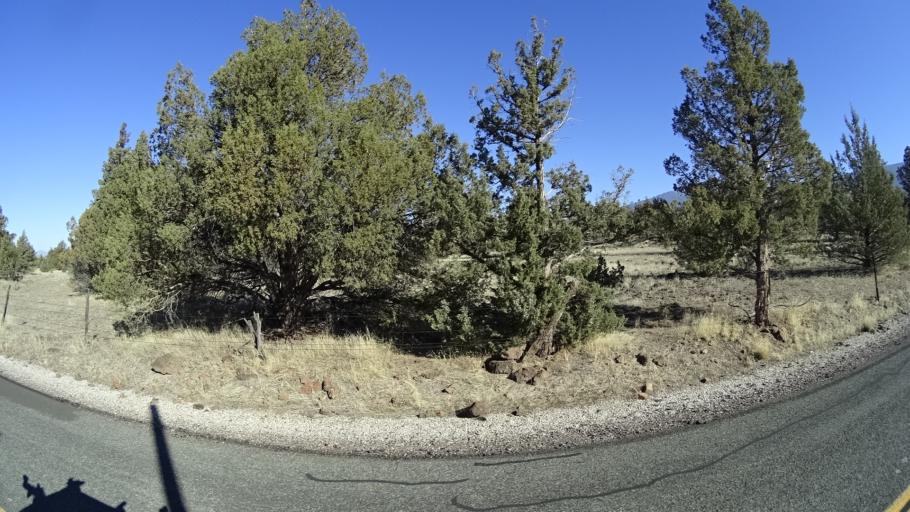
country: US
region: California
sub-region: Siskiyou County
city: Montague
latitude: 41.6462
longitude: -122.3580
